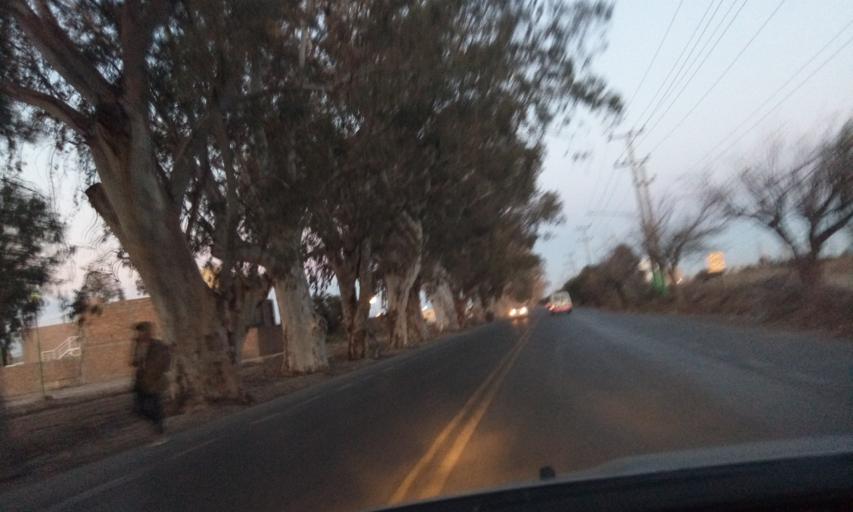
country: AR
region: San Juan
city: San Juan
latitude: -31.5478
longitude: -68.5797
